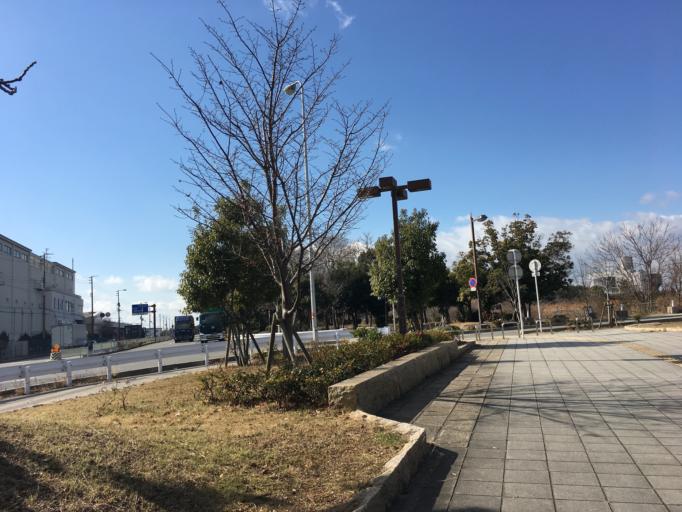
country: JP
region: Hyogo
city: Amagasaki
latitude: 34.6386
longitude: 135.4067
